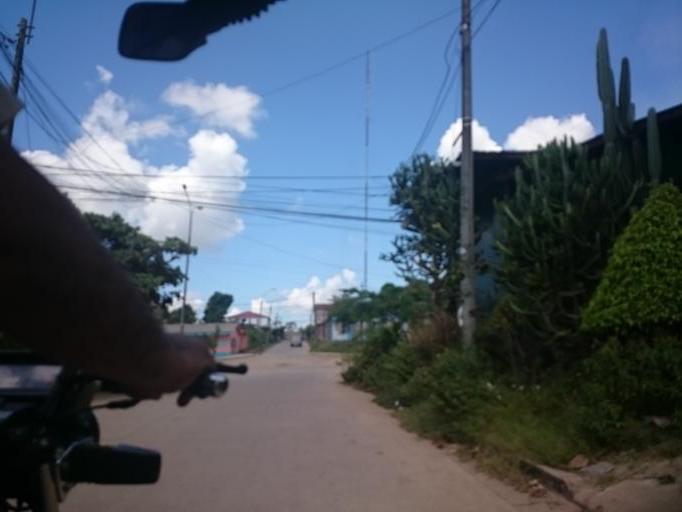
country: PE
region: Ucayali
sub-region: Provincia de Coronel Portillo
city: Pucallpa
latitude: -8.3739
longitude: -74.5344
